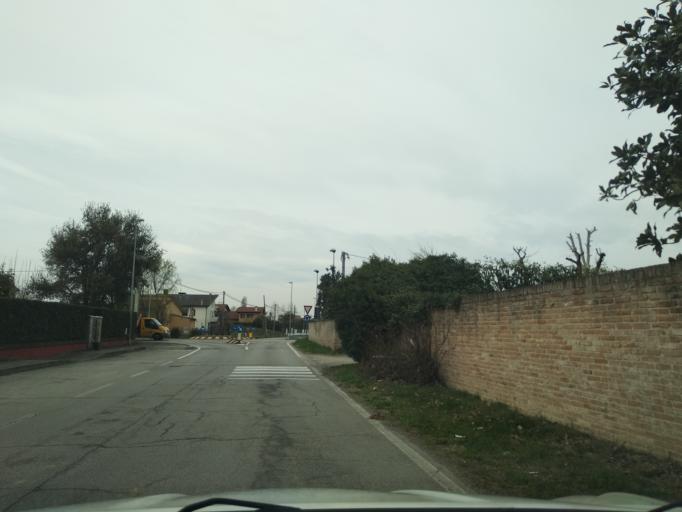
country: IT
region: Veneto
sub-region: Provincia di Padova
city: Selvazzano Dentro
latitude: 45.4025
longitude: 11.7833
